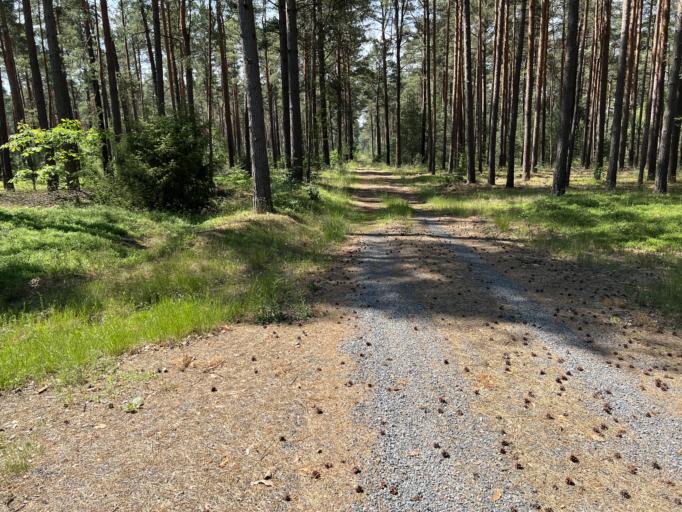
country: DE
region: Brandenburg
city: Teupitz
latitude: 52.0743
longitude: 13.6176
